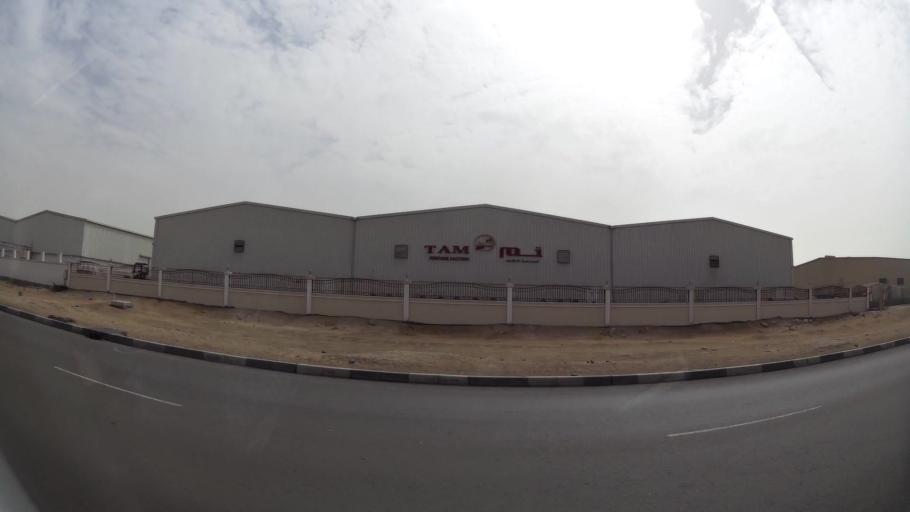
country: AE
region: Abu Dhabi
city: Abu Dhabi
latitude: 24.3234
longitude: 54.5062
